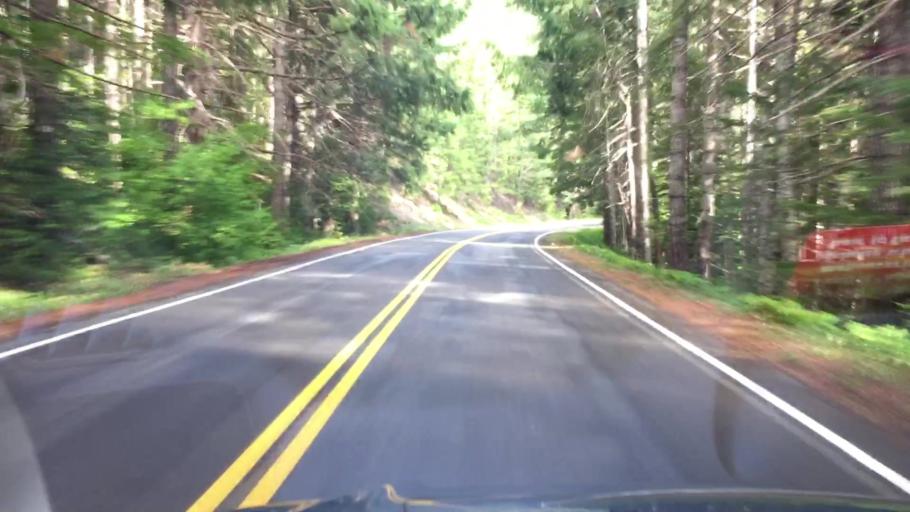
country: US
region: Washington
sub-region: Pierce County
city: Buckley
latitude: 46.7424
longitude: -121.6166
